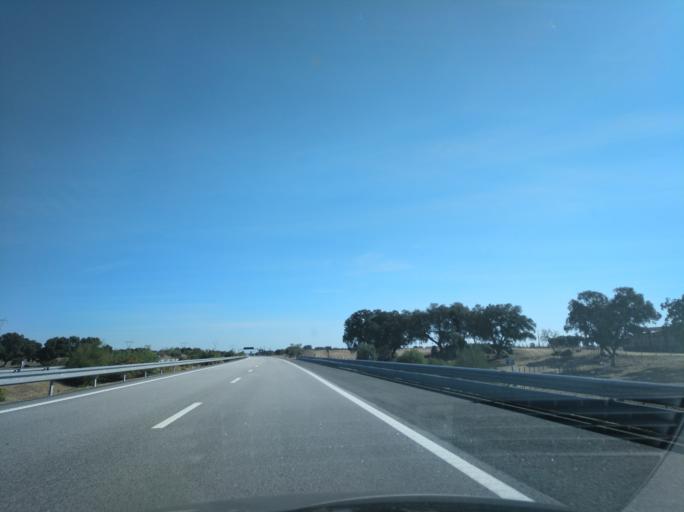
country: PT
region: Evora
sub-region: Evora
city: Evora
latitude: 38.6328
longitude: -7.8870
